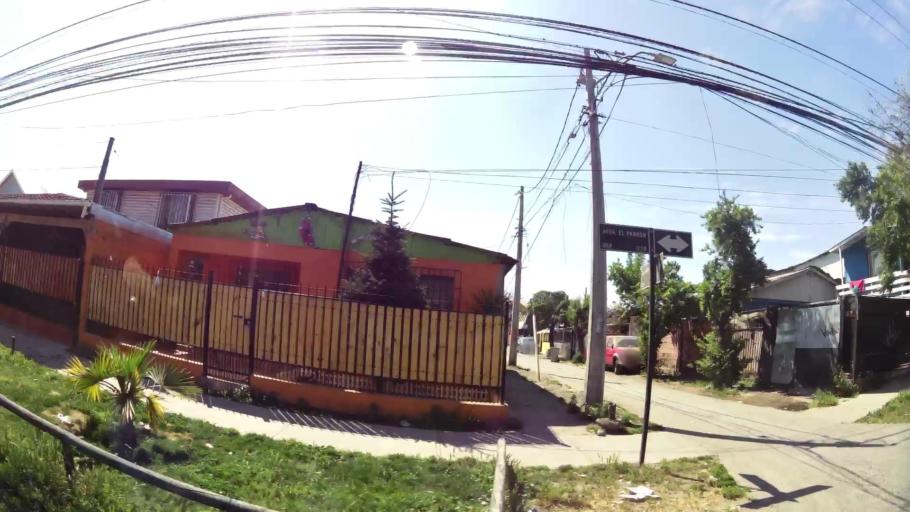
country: CL
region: Santiago Metropolitan
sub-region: Provincia de Santiago
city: La Pintana
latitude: -33.5284
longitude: -70.6495
